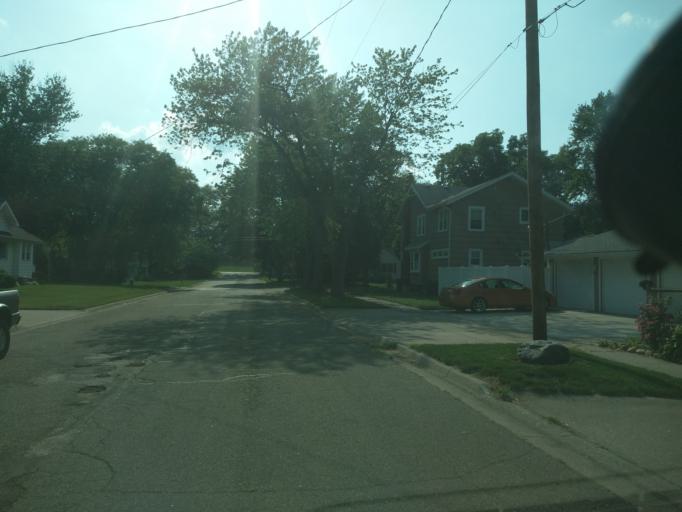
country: US
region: Michigan
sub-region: Jackson County
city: Jackson
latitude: 42.2494
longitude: -84.4312
